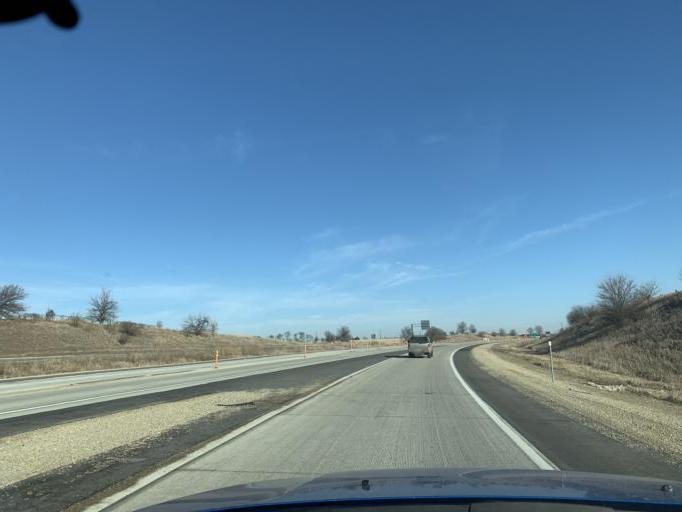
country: US
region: Wisconsin
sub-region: Green County
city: Monroe
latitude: 42.6153
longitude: -89.6496
